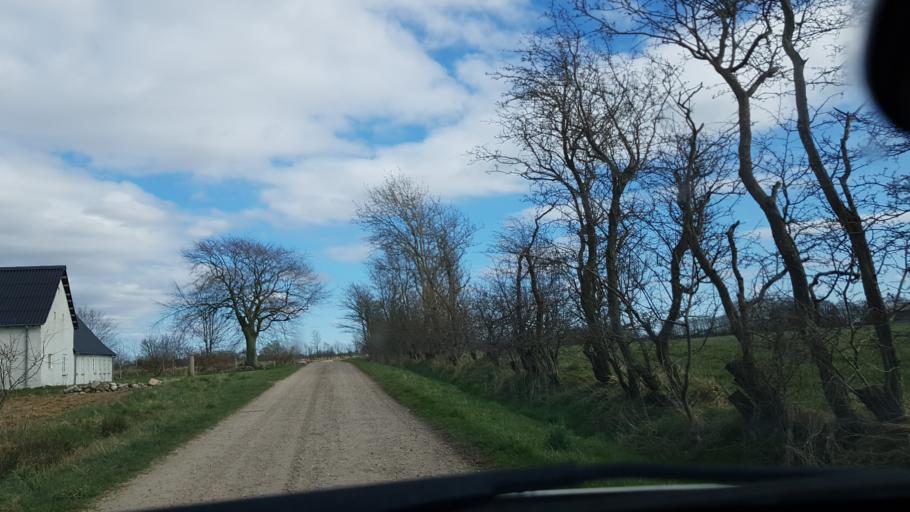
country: DK
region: South Denmark
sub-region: Esbjerg Kommune
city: Ribe
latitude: 55.2849
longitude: 8.8055
